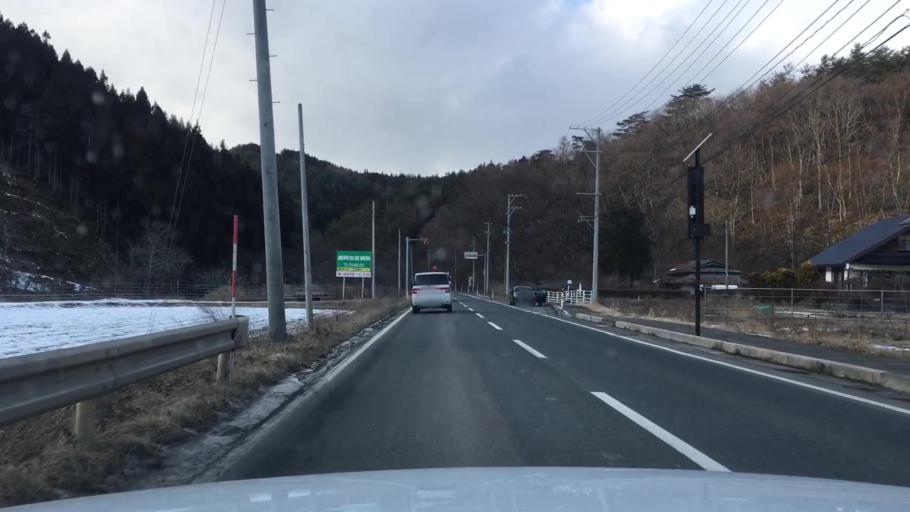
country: JP
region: Iwate
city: Morioka-shi
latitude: 39.6750
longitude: 141.2285
